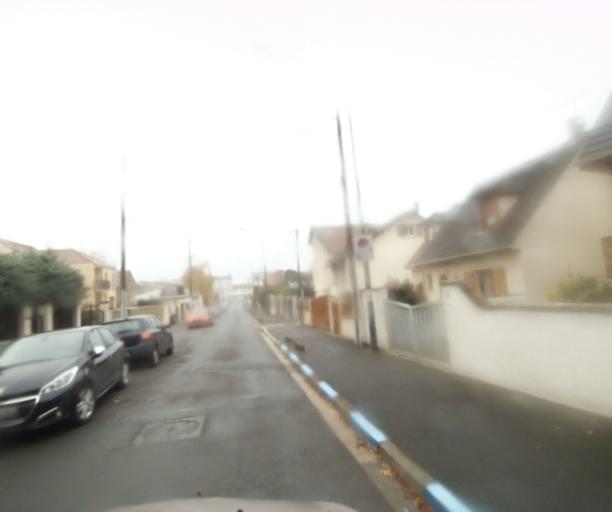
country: FR
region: Ile-de-France
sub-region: Departement de Seine-Saint-Denis
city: Tremblay-en-France
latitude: 48.9417
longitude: 2.5671
